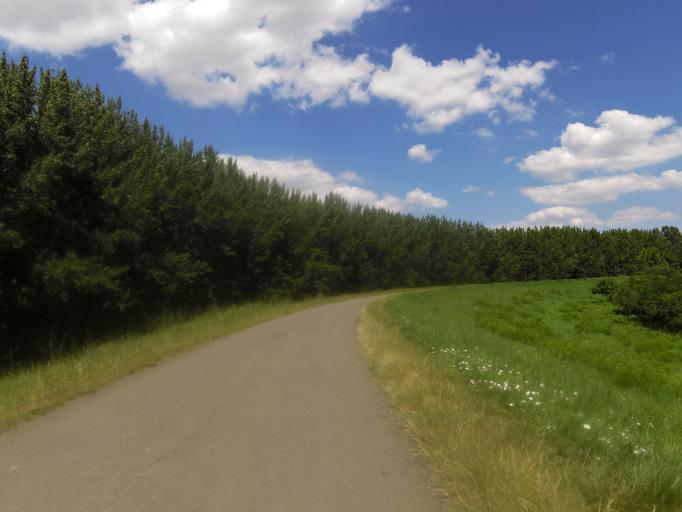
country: HU
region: Heves
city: Tiszanana
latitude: 47.5709
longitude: 20.6057
